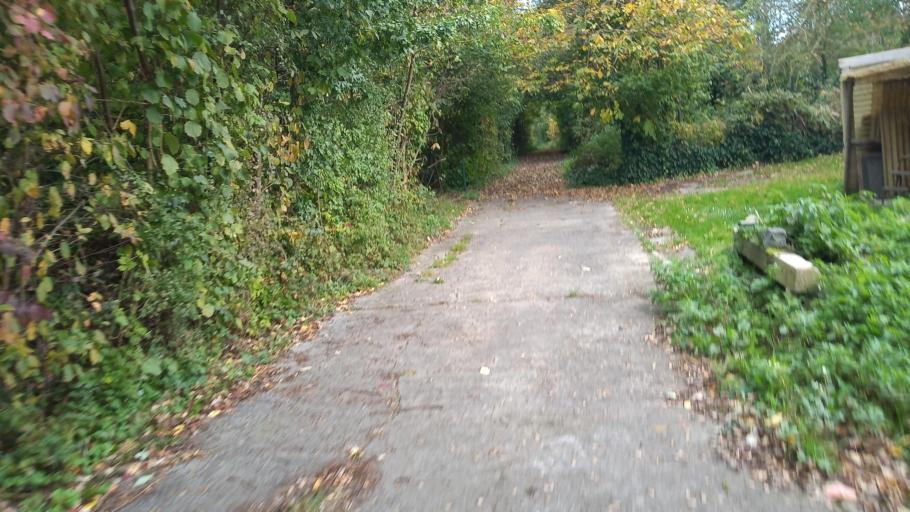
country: BE
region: Flanders
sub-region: Provincie West-Vlaanderen
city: Kortrijk
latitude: 50.8106
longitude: 3.2251
